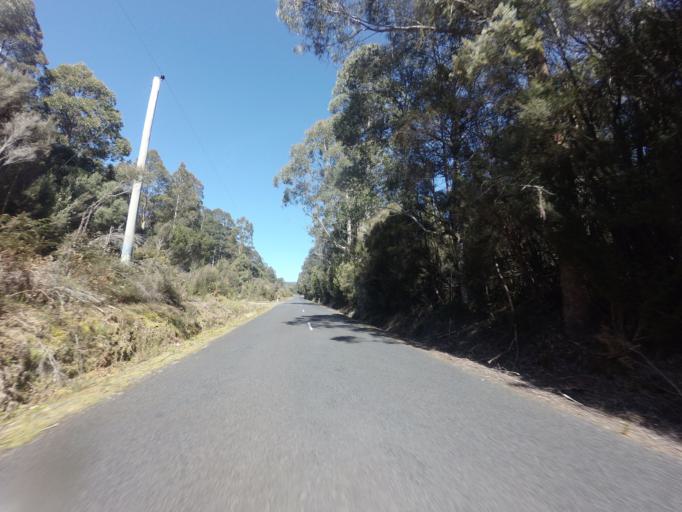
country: AU
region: Tasmania
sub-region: Derwent Valley
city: New Norfolk
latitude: -42.7662
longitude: 146.5559
